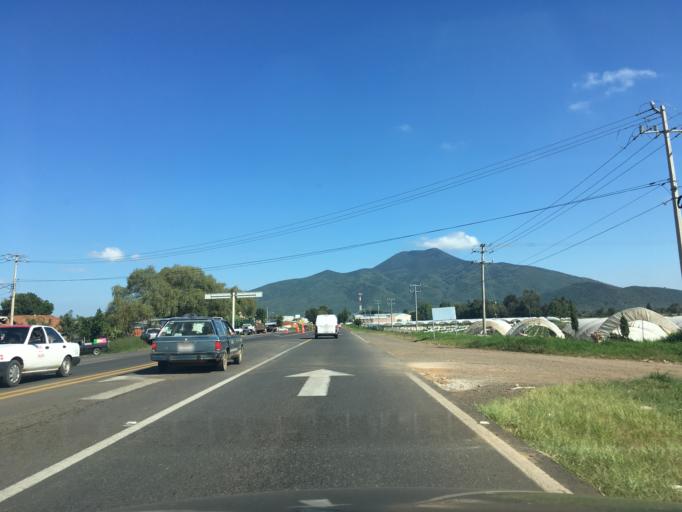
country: MX
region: Mexico
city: Tangancicuaro de Arista
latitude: 19.8785
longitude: -102.1987
